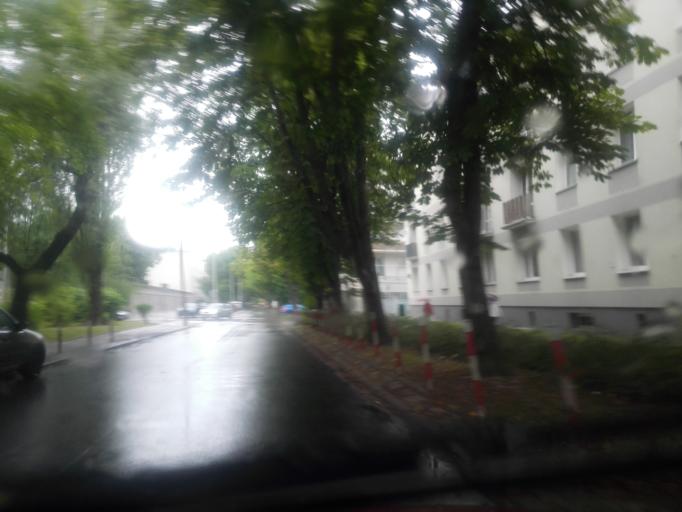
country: PL
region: Masovian Voivodeship
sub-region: Warszawa
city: Mokotow
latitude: 52.1928
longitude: 21.0105
